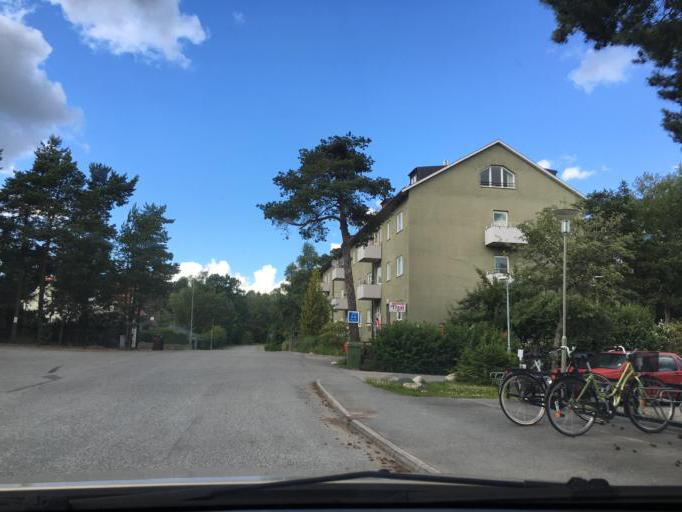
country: SE
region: Stockholm
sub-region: Nacka Kommun
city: Boo
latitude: 59.3191
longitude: 18.2433
